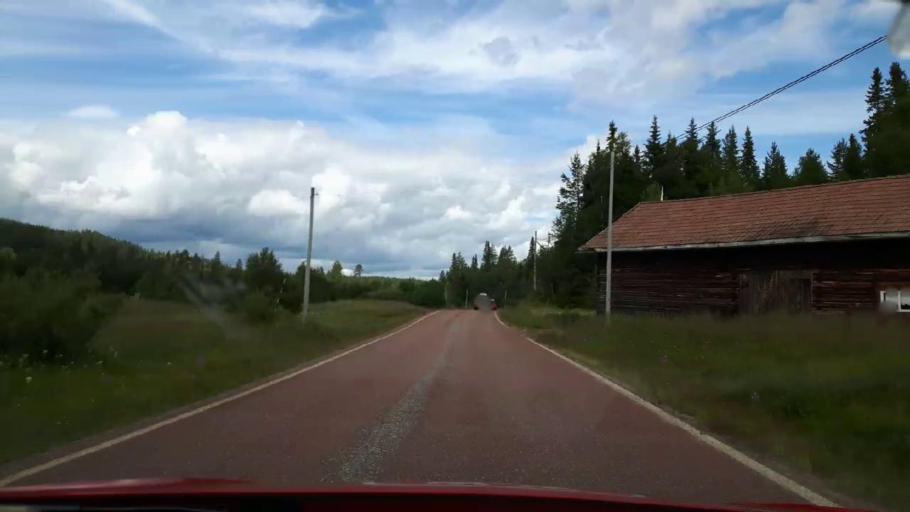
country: NO
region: Hedmark
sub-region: Trysil
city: Innbygda
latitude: 61.9975
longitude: 12.9811
